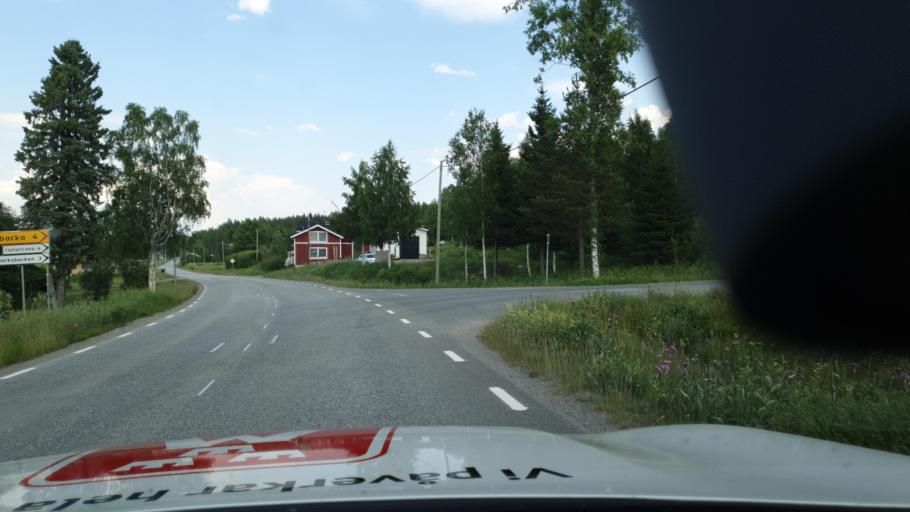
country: SE
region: Vaesterbotten
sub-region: Skelleftea Kommun
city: Viken
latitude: 64.7341
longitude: 20.7446
